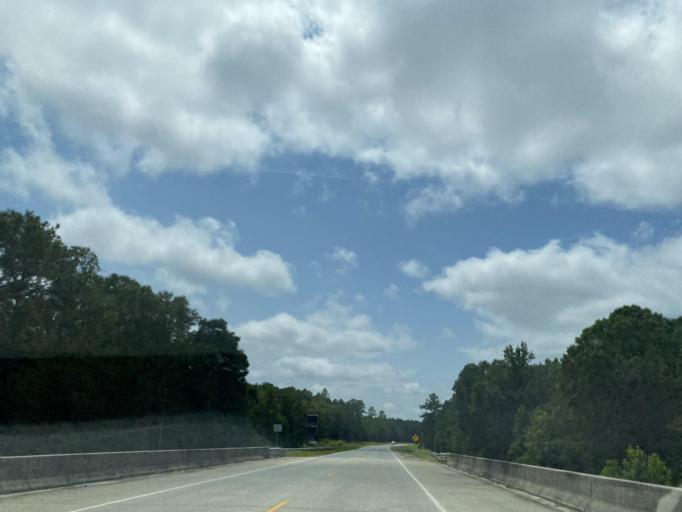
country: US
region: Georgia
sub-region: Wheeler County
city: Alamo
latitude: 32.1291
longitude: -82.7862
